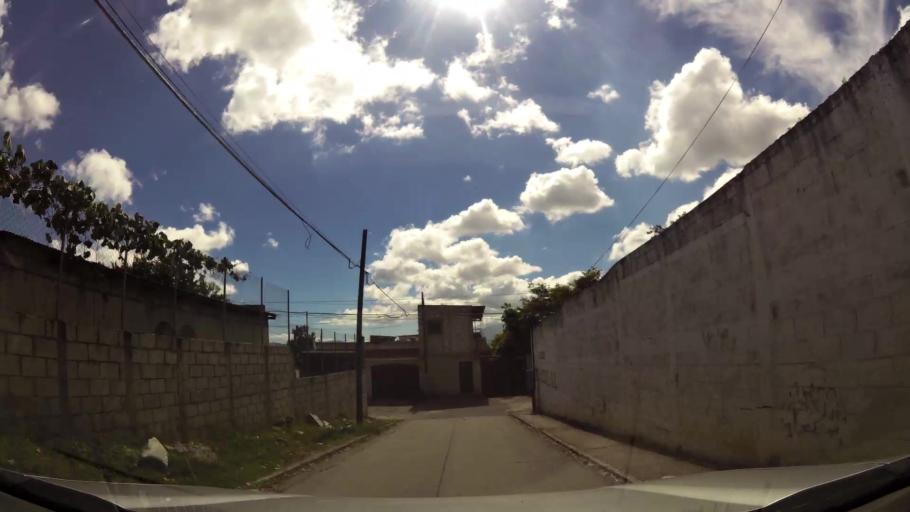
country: GT
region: Guatemala
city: Petapa
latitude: 14.5488
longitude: -90.5440
